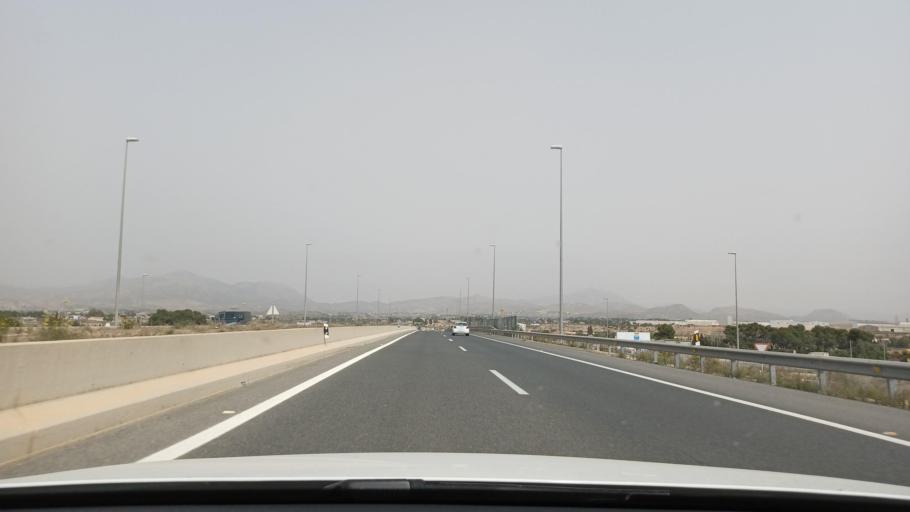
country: ES
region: Valencia
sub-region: Provincia de Alicante
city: San Vicent del Raspeig
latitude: 38.3950
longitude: -0.5477
